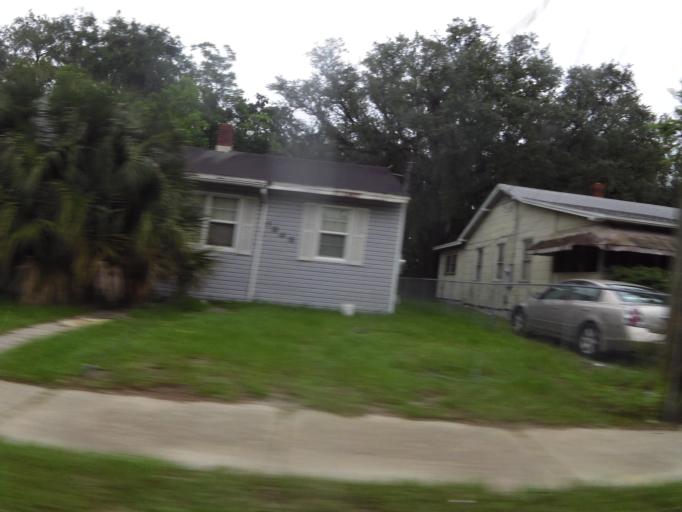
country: US
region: Florida
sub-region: Duval County
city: Jacksonville
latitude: 30.3471
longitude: -81.6332
